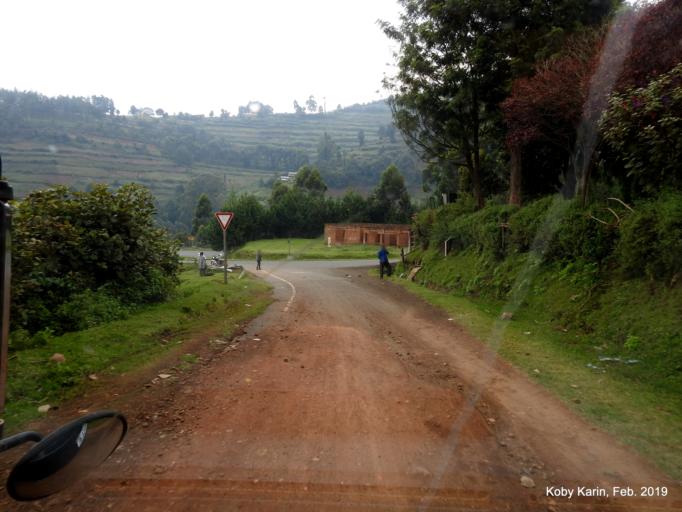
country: UG
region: Western Region
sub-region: Kisoro District
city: Kisoro
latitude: -1.2046
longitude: 29.8019
